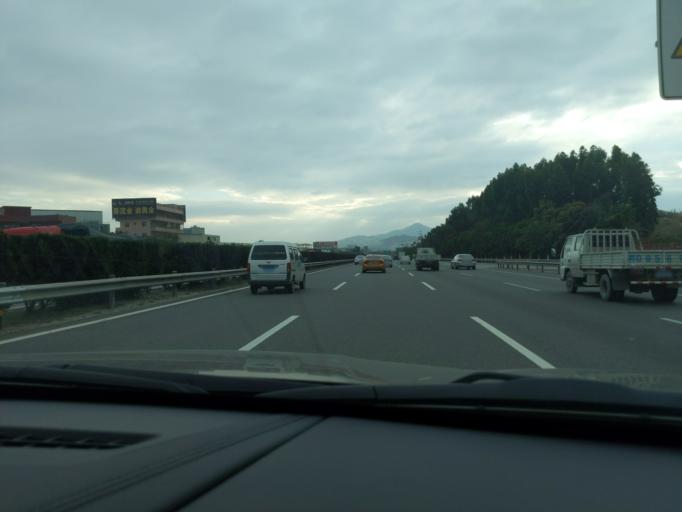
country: CN
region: Fujian
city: Anhai
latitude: 24.7158
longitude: 118.3990
